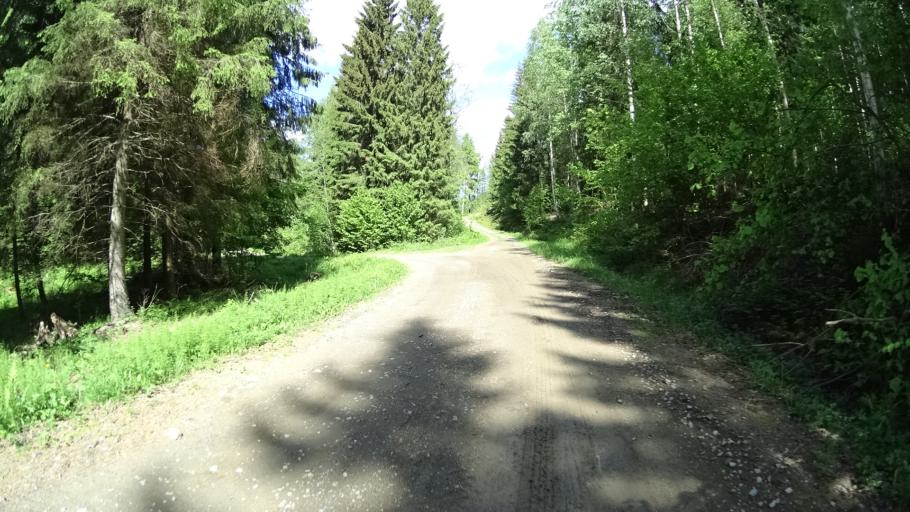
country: FI
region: Uusimaa
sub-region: Raaseporin
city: Karis
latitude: 60.1496
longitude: 23.6251
